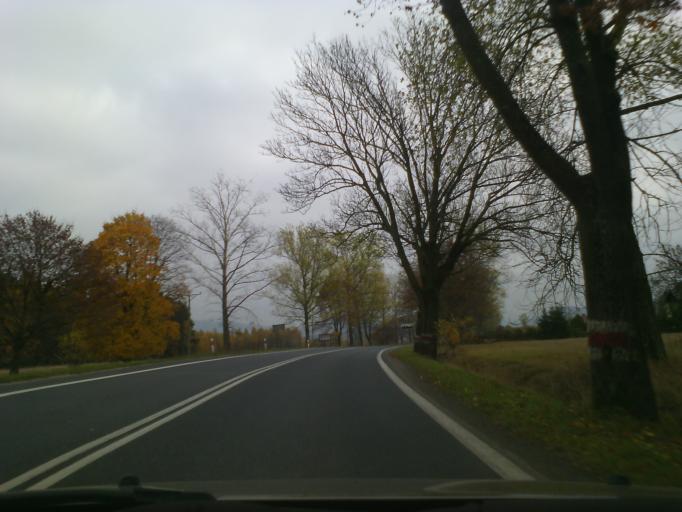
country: PL
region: Lower Silesian Voivodeship
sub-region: Powiat walbrzyski
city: Czarny Bor
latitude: 50.7817
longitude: 16.1008
